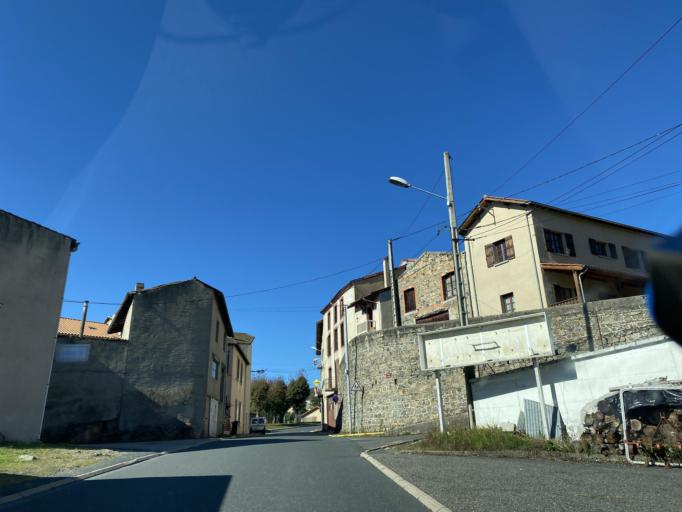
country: FR
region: Rhone-Alpes
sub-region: Departement de la Loire
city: Saint-Just-en-Chevalet
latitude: 45.9150
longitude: 3.8462
